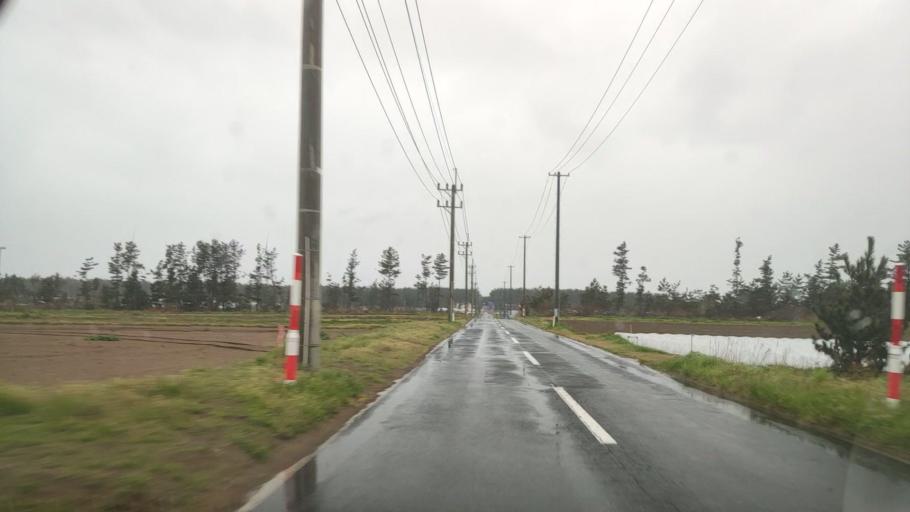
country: JP
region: Akita
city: Noshiromachi
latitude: 40.0962
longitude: 139.9715
